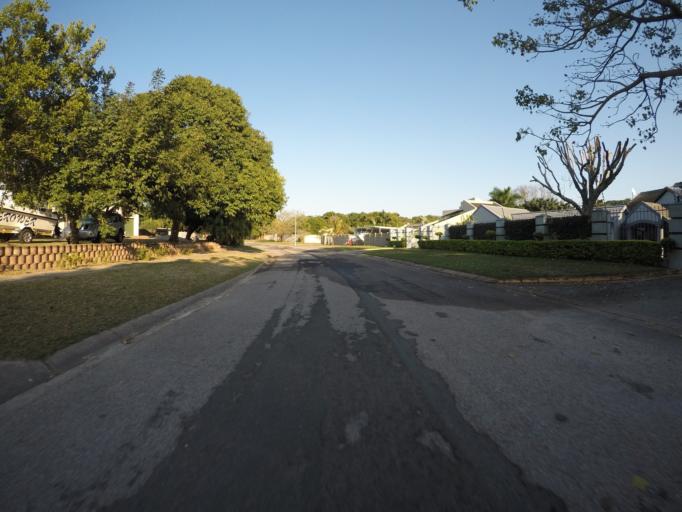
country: ZA
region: KwaZulu-Natal
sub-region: uThungulu District Municipality
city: Richards Bay
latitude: -28.7751
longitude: 32.1027
